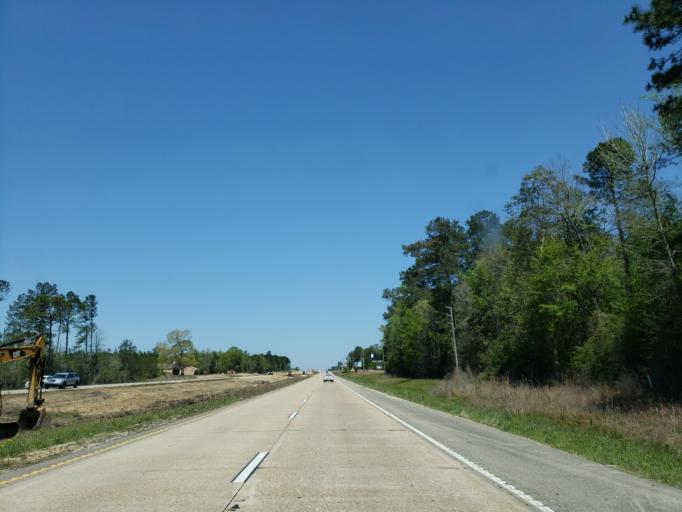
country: US
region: Mississippi
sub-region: Stone County
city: Wiggins
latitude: 31.0598
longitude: -89.2067
